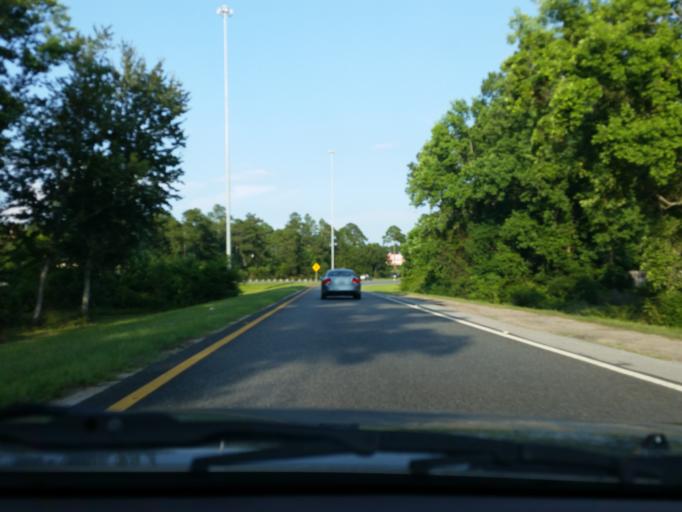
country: US
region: Florida
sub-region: Escambia County
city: Ensley
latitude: 30.5196
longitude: -87.3121
